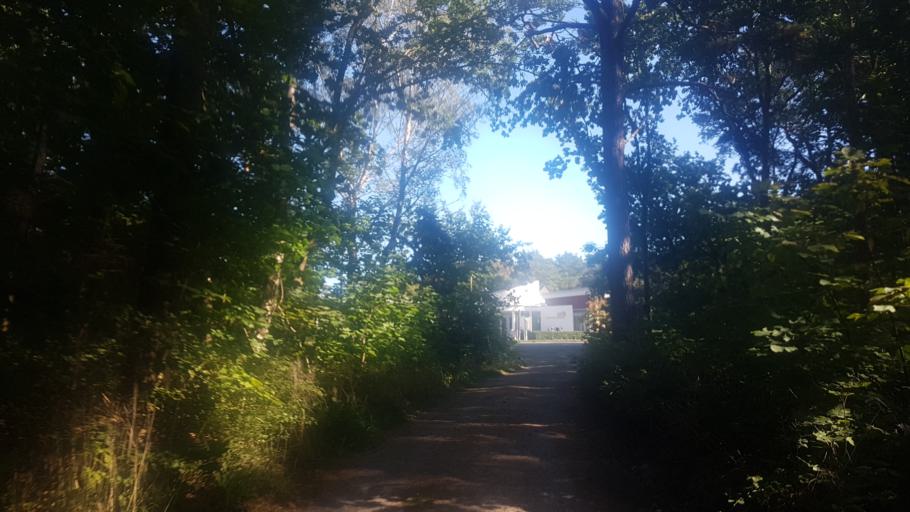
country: DE
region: Mecklenburg-Vorpommern
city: Altenkirchen
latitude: 54.6192
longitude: 13.3753
